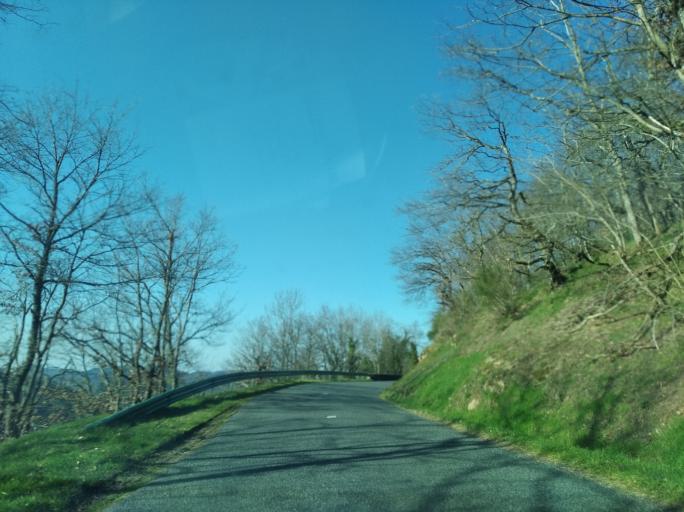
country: FR
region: Auvergne
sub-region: Departement de l'Allier
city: Le Mayet-de-Montagne
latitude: 46.1062
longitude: 3.6803
